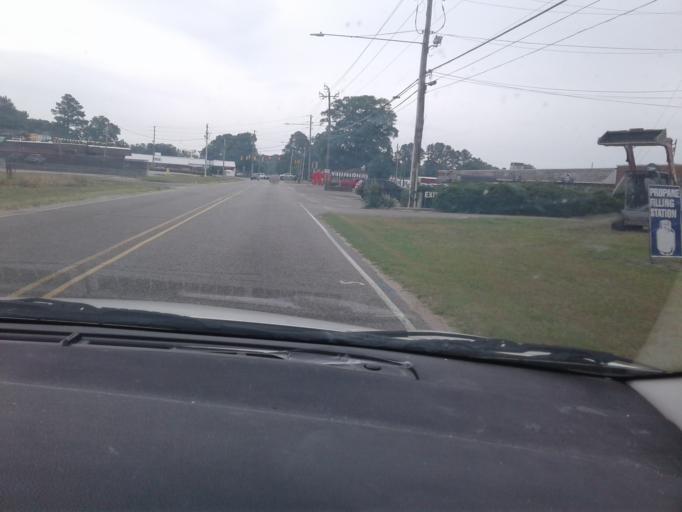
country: US
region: North Carolina
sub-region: Harnett County
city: Dunn
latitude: 35.3163
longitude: -78.6305
